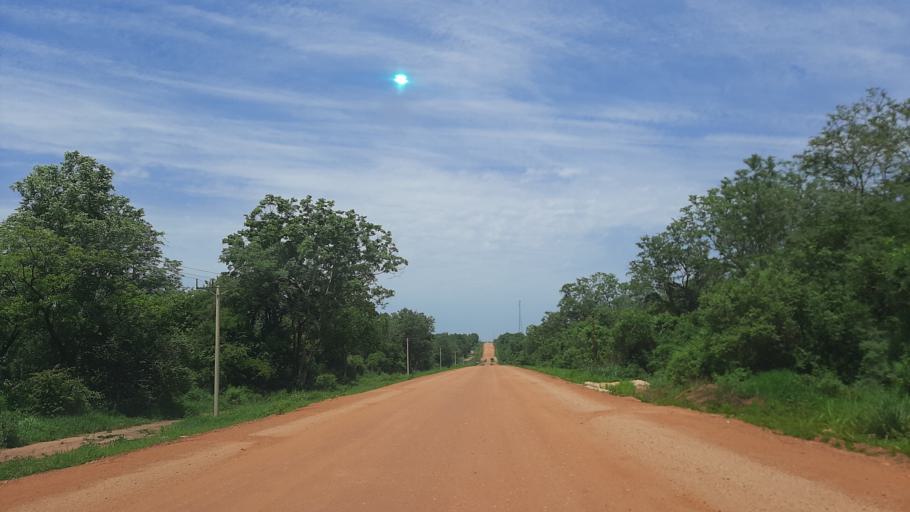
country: ET
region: Gambela
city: Gambela
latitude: 8.0721
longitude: 34.5886
